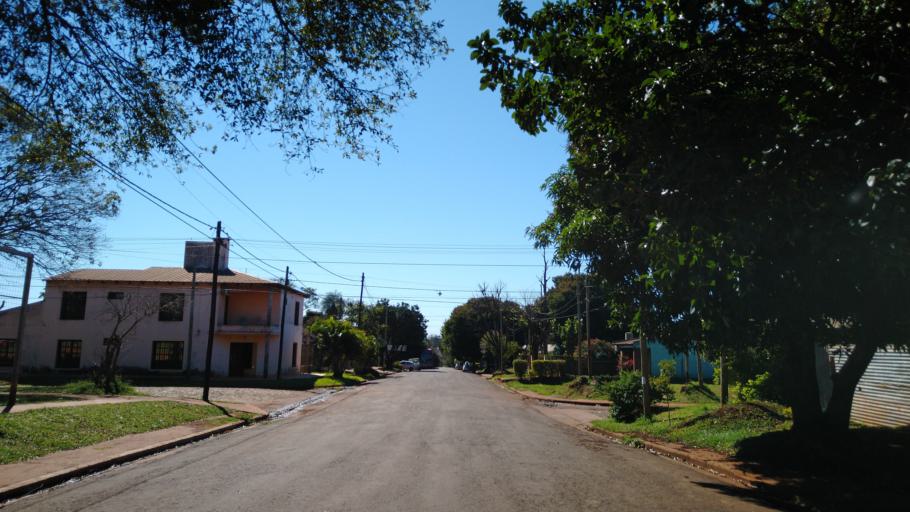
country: AR
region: Misiones
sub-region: Departamento de Capital
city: Posadas
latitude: -27.3986
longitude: -55.9342
